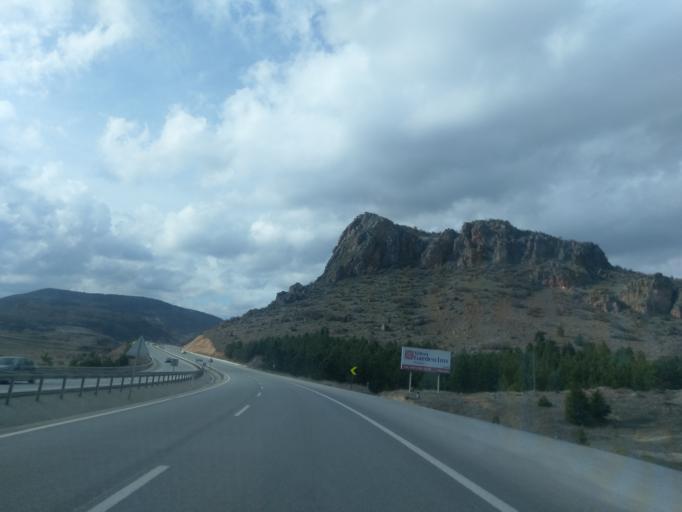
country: TR
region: Kuetahya
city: Sabuncu
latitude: 39.5734
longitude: 30.1019
